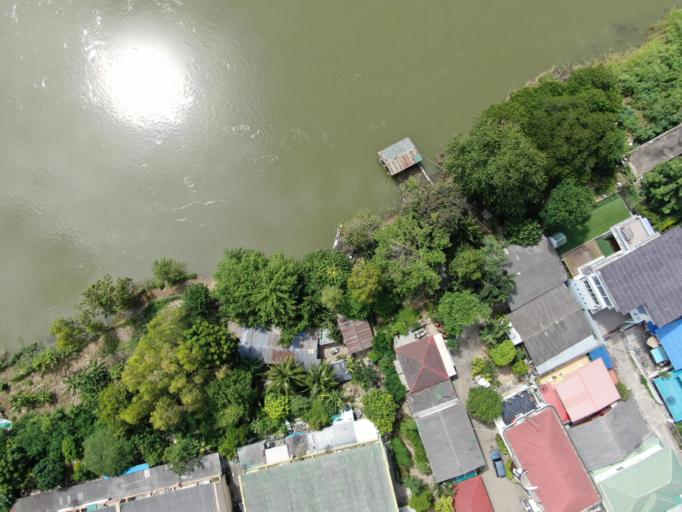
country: TH
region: Ratchaburi
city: Ban Pong
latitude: 13.8068
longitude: 99.8729
